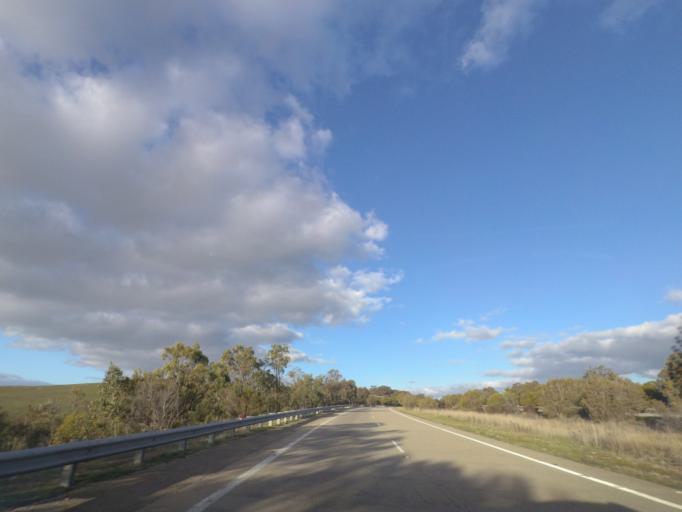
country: AU
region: New South Wales
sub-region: Yass Valley
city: Yass
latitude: -34.8029
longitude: 148.5551
